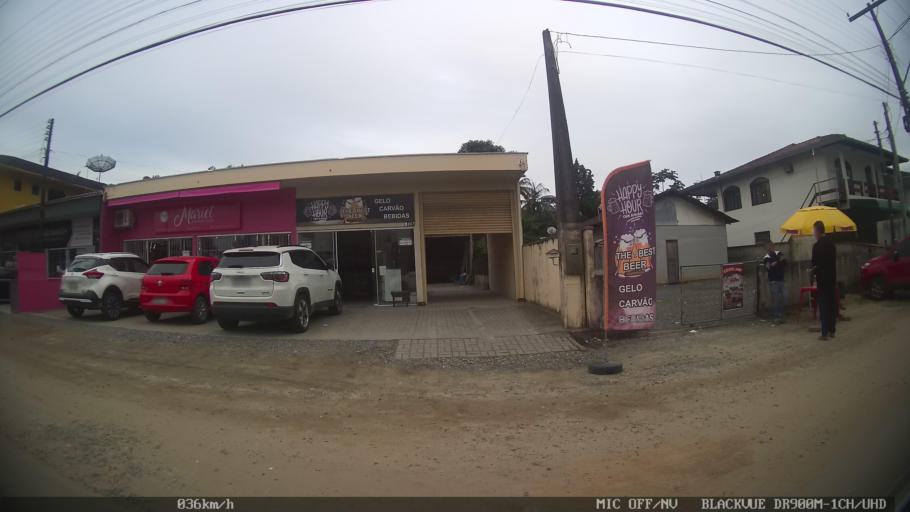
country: BR
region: Santa Catarina
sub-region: Joinville
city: Joinville
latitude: -26.3369
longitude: -48.9048
